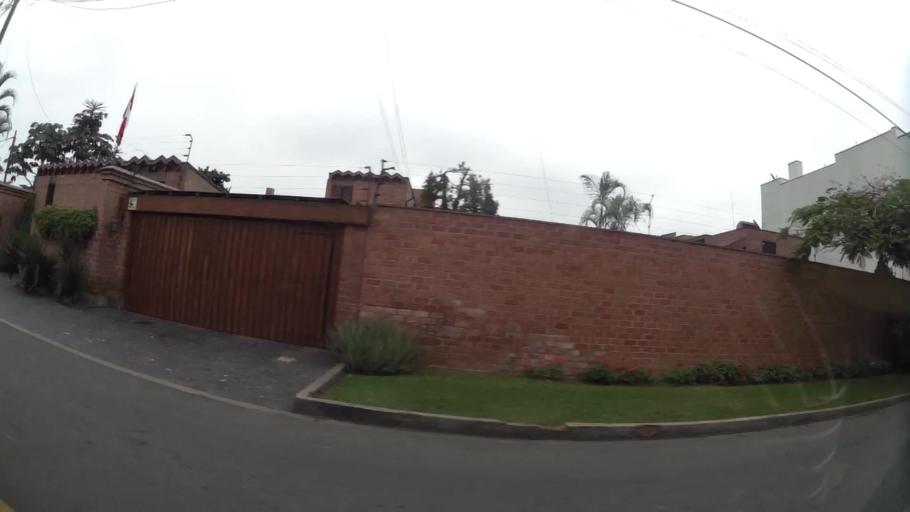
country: PE
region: Lima
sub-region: Lima
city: La Molina
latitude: -12.0696
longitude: -76.9639
